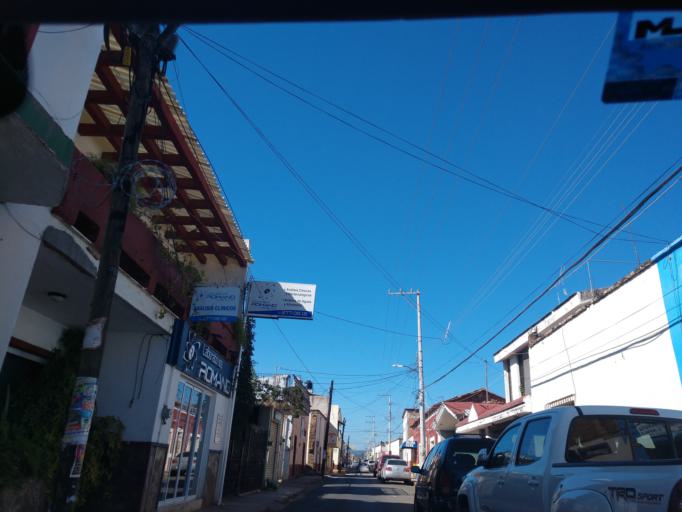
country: MX
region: Nayarit
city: Compostela
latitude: 21.2372
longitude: -104.9016
